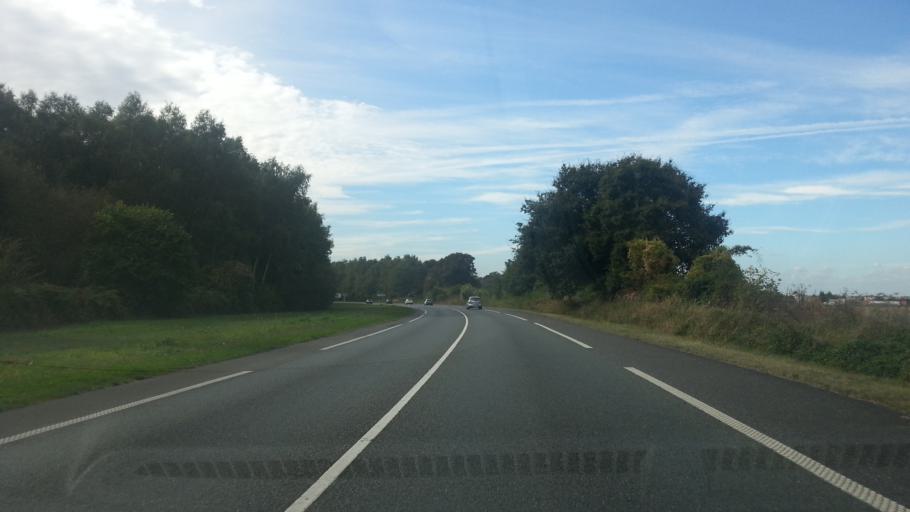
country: FR
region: Picardie
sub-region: Departement de l'Oise
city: Creil
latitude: 49.2455
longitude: 2.4901
